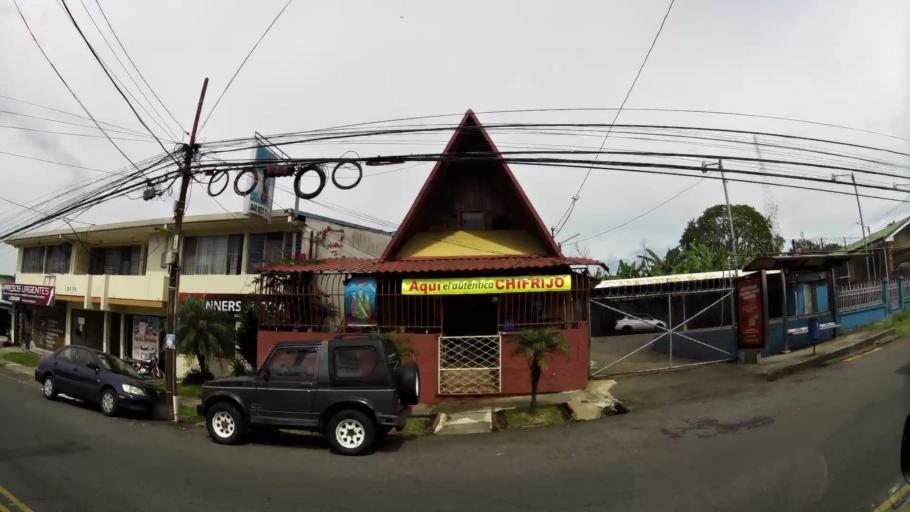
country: CR
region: San Jose
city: San Pedro
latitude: 9.9251
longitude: -84.0601
